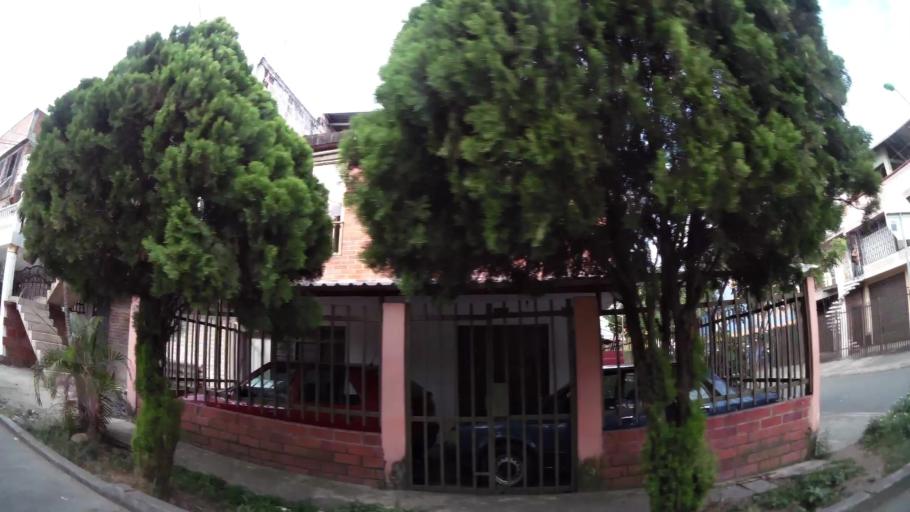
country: CO
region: Valle del Cauca
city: Cali
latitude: 3.4690
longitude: -76.4939
